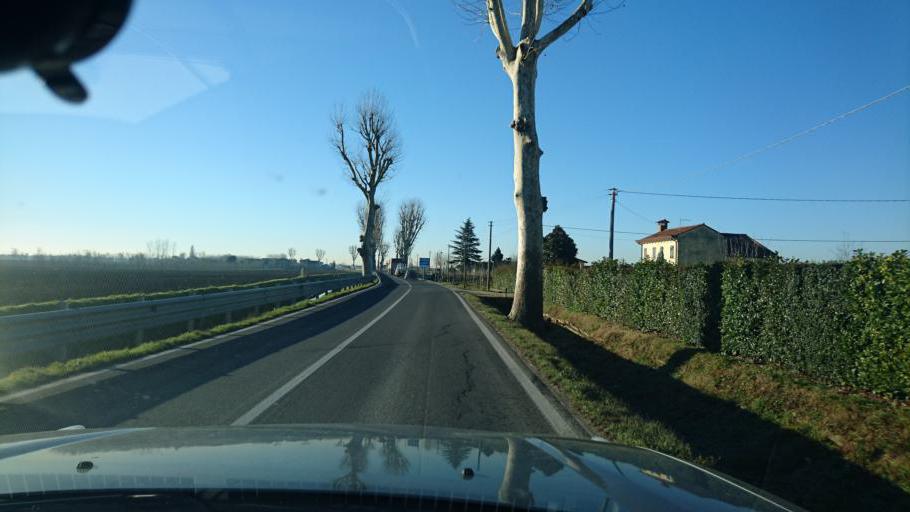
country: IT
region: Veneto
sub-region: Provincia di Padova
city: Pontelongo
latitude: 45.2313
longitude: 12.0226
